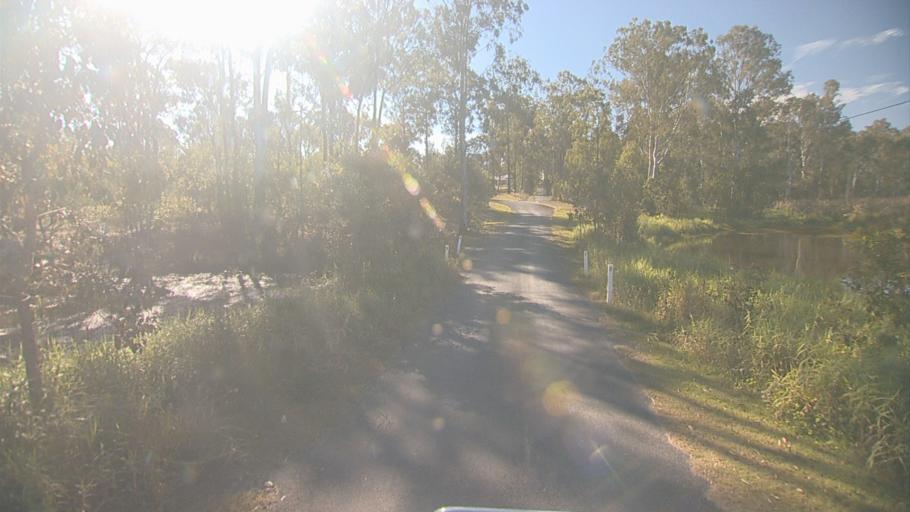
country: AU
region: Queensland
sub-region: Ipswich
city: Springfield Lakes
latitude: -27.7385
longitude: 152.9219
